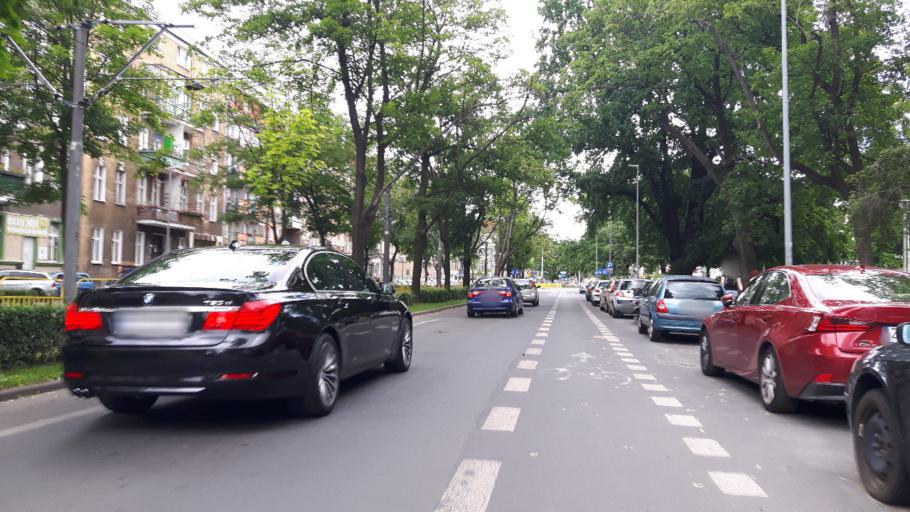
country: PL
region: West Pomeranian Voivodeship
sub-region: Szczecin
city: Szczecin
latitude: 53.4257
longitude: 14.5348
